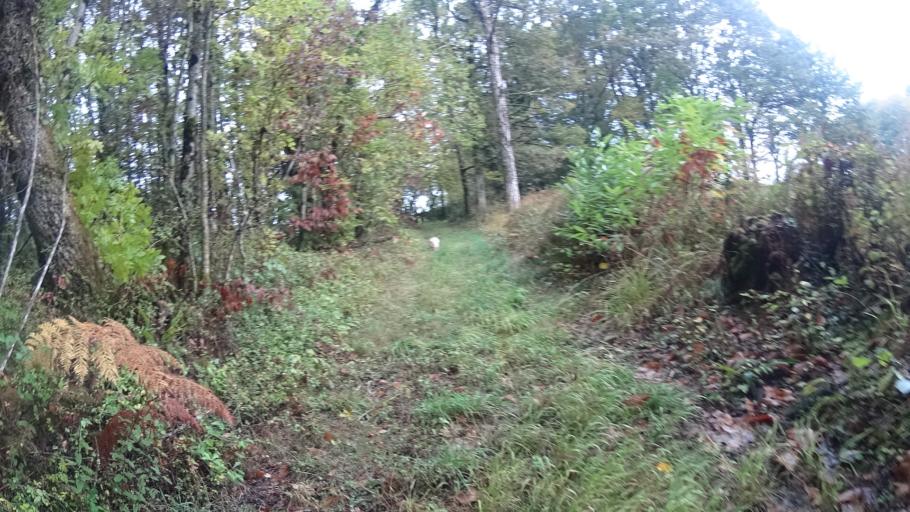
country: FR
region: Aquitaine
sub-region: Departement de la Dordogne
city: Payzac
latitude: 45.3580
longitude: 1.2053
